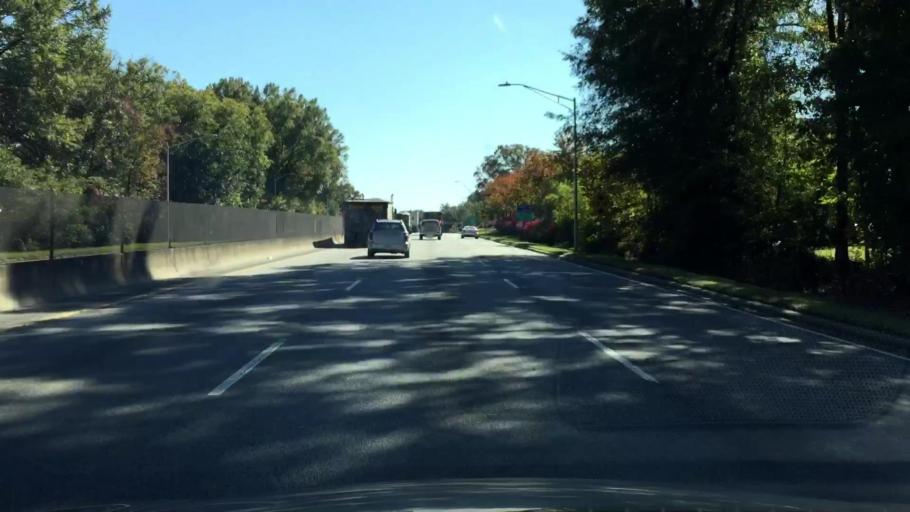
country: US
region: North Carolina
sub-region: Guilford County
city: Greensboro
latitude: 36.0772
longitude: -79.7670
